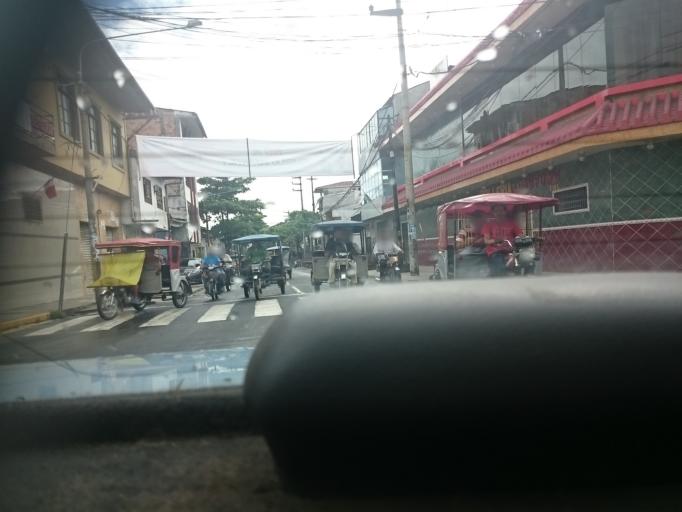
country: PE
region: Loreto
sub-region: Provincia de Maynas
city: Iquitos
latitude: -3.7537
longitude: -73.2495
